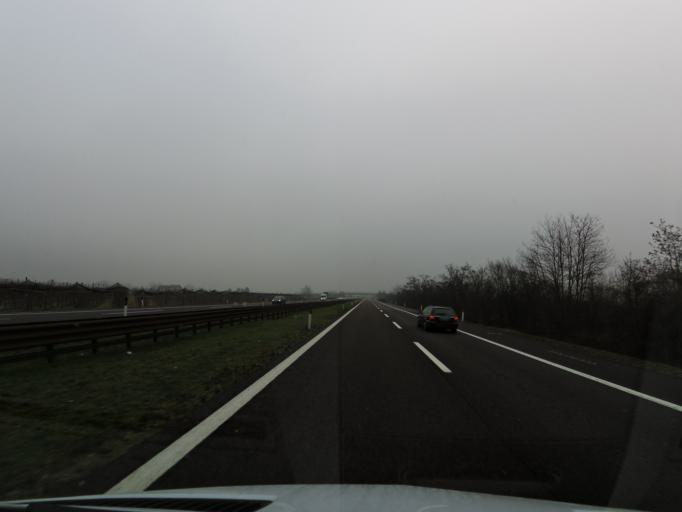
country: IT
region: Veneto
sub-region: Provincia di Verona
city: Alpo
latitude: 45.3783
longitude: 10.9129
